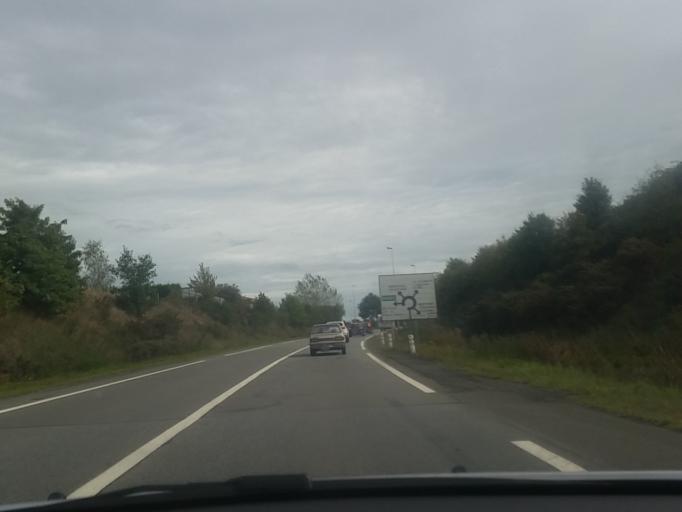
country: FR
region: Brittany
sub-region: Departement d'Ille-et-Vilaine
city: Martigne-Ferchaud
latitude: 47.8403
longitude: -1.3271
